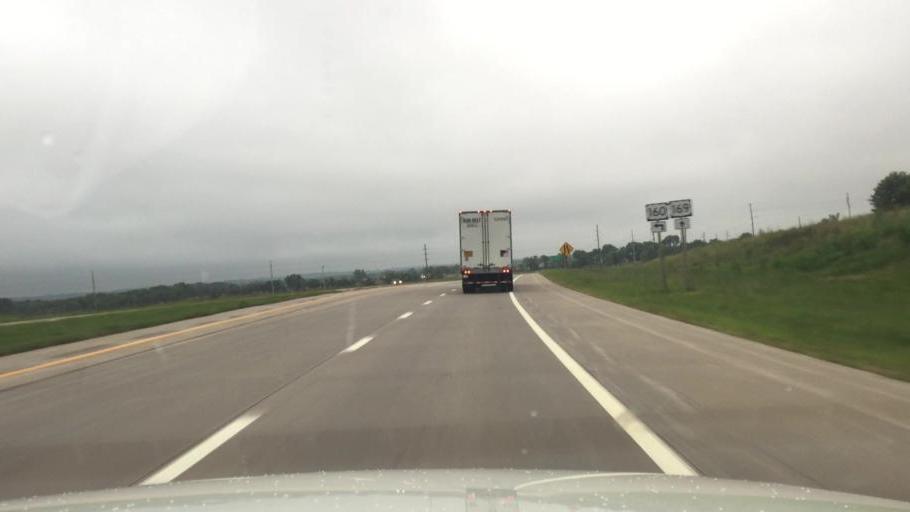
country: US
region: Kansas
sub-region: Montgomery County
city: Cherryvale
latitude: 37.2121
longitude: -95.5852
